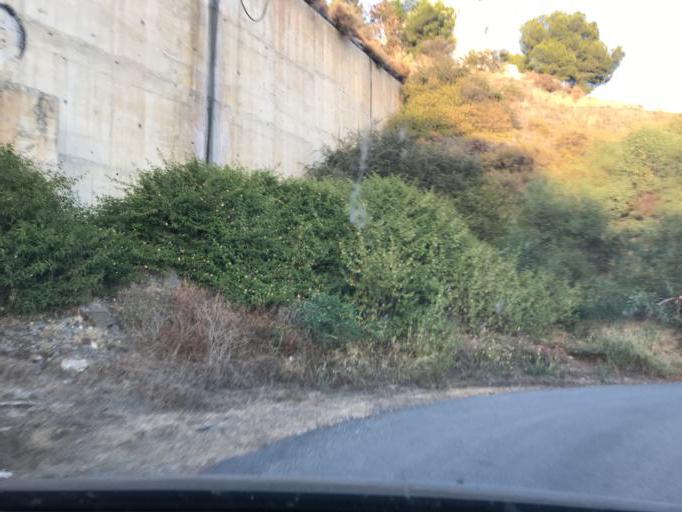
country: ES
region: Andalusia
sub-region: Provincia de Granada
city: Salobrena
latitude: 36.7435
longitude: -3.6176
